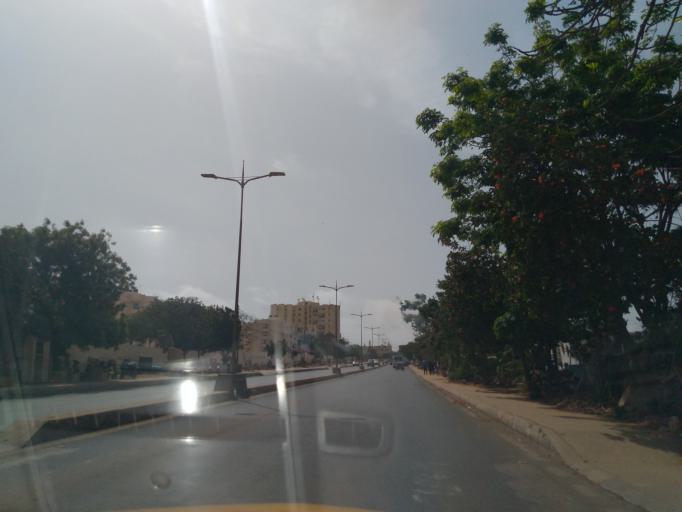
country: SN
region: Dakar
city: Mermoz Boabab
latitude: 14.7066
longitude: -17.4792
